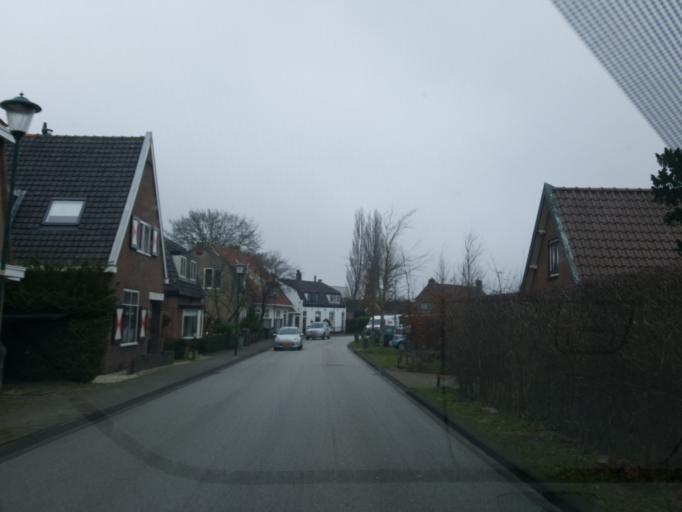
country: NL
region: North Holland
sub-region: Gemeente Wijdemeren
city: Kortenhoef
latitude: 52.2558
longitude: 5.1209
